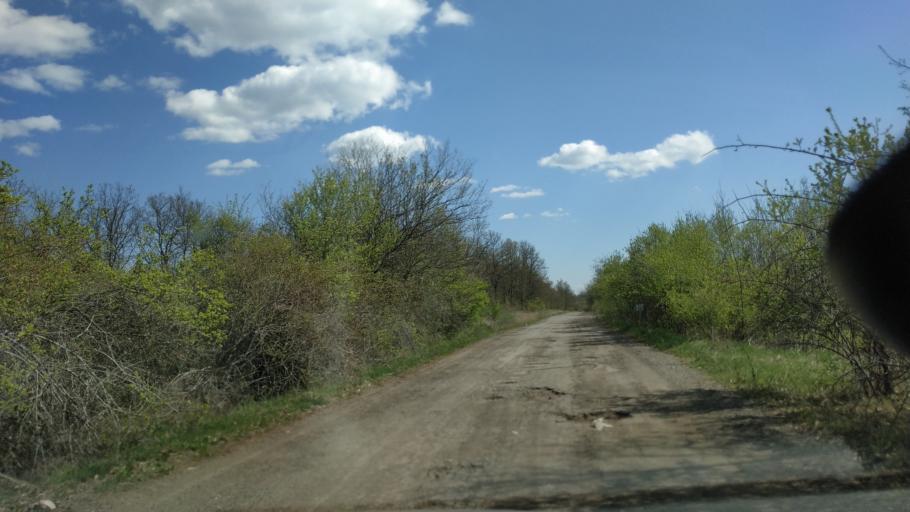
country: RS
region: Central Serbia
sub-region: Zajecarski Okrug
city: Soko Banja
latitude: 43.5329
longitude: 21.9063
